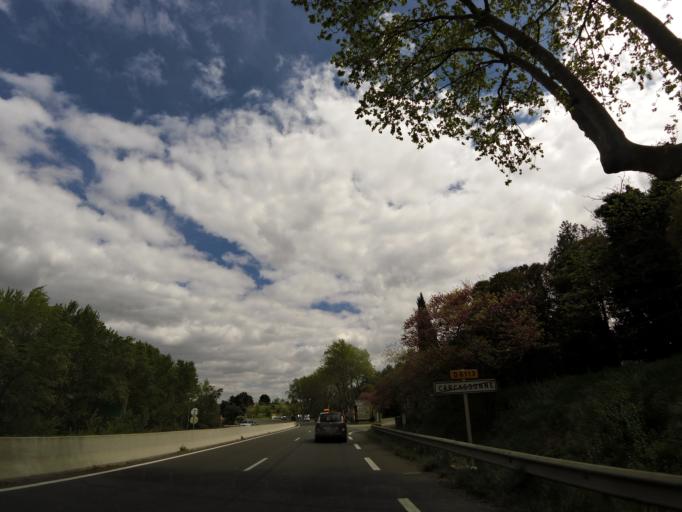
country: FR
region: Languedoc-Roussillon
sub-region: Departement de l'Aude
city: Palaja
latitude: 43.2047
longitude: 2.3996
